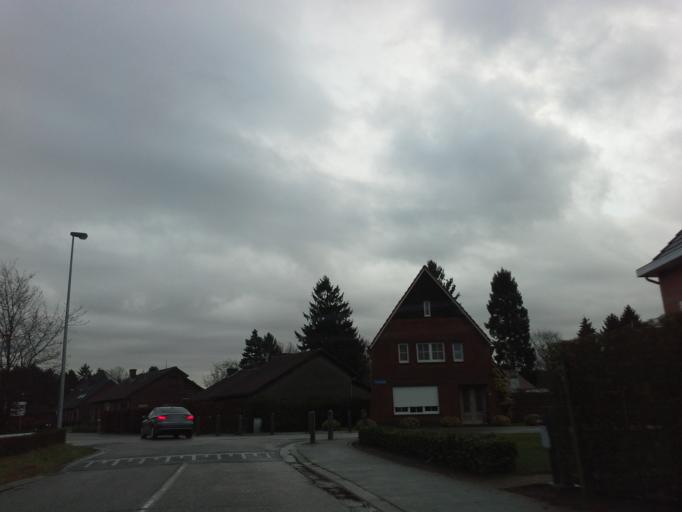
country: BE
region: Flanders
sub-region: Provincie Antwerpen
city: Meerhout
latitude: 51.1363
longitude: 5.0745
